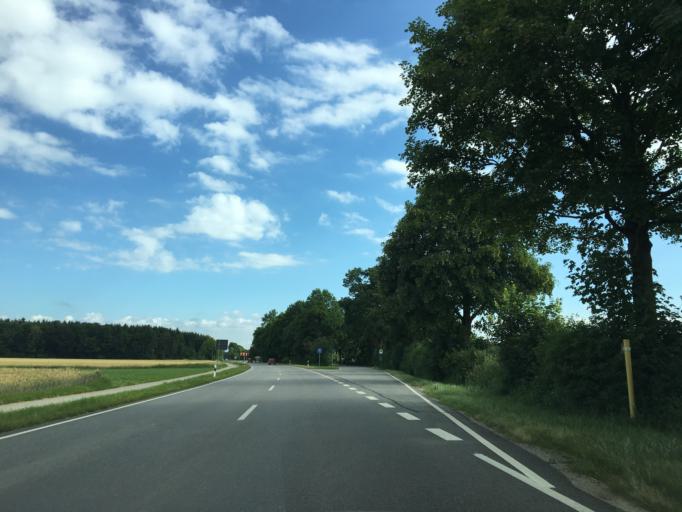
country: DE
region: Bavaria
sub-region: Upper Bavaria
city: Sauerlach
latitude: 47.9549
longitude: 11.6519
